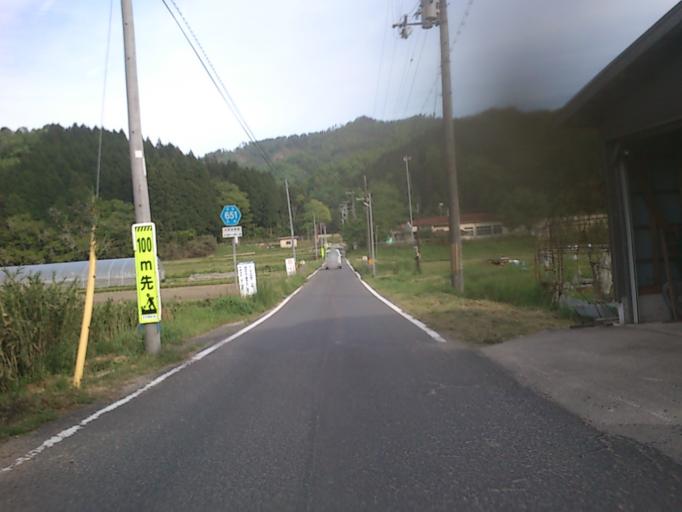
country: JP
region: Kyoto
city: Miyazu
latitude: 35.5691
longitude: 135.1162
